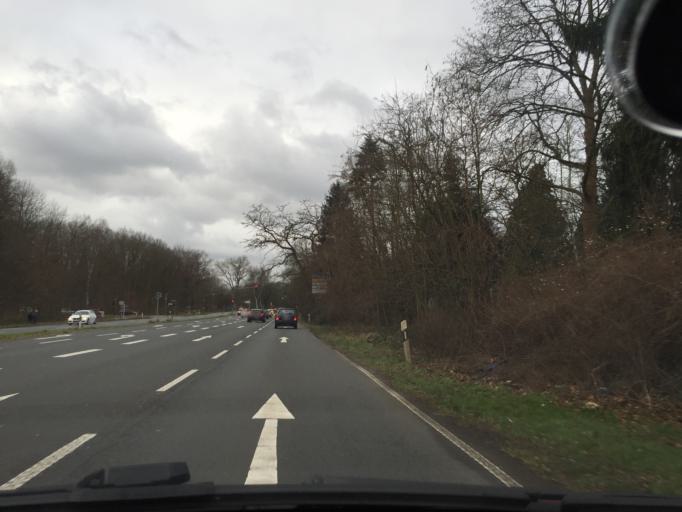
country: DE
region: North Rhine-Westphalia
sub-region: Regierungsbezirk Koln
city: Bayenthal
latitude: 50.8960
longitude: 6.9776
